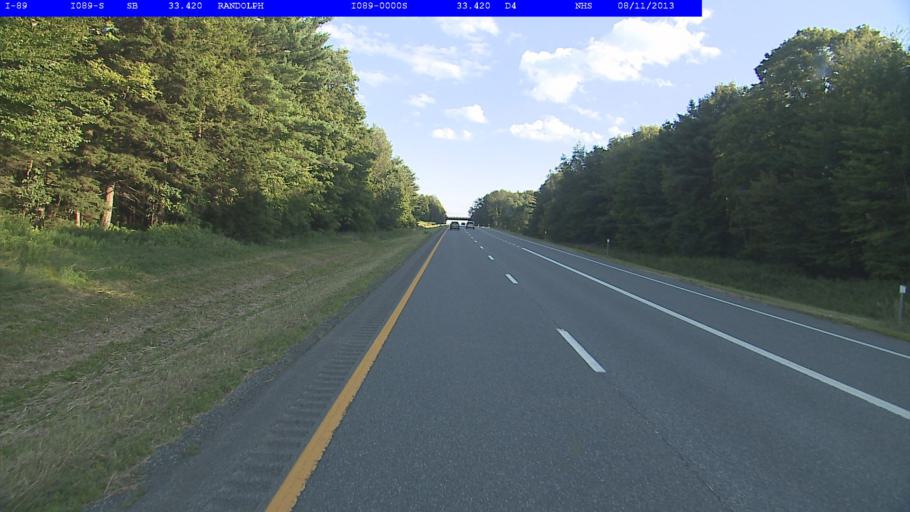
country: US
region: Vermont
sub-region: Orange County
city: Randolph
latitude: 43.9814
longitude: -72.6274
